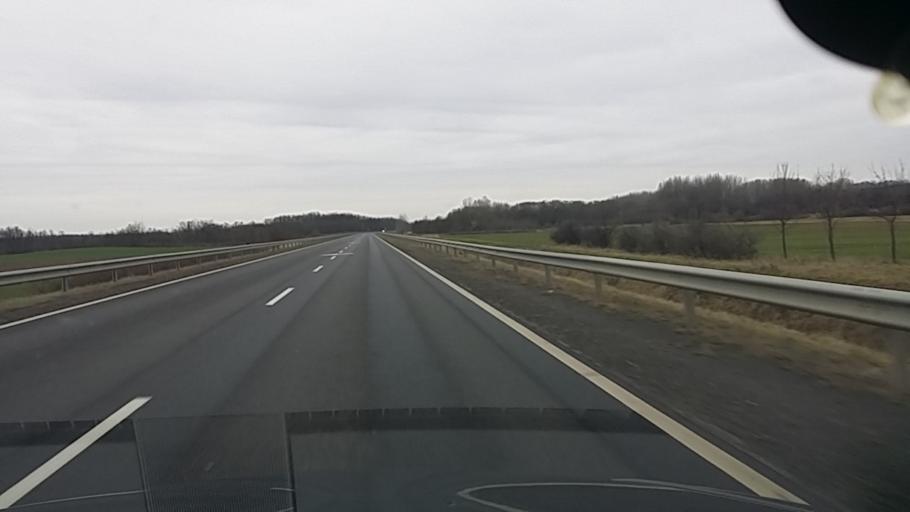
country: HU
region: Szabolcs-Szatmar-Bereg
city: Napkor
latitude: 47.9325
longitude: 21.8189
